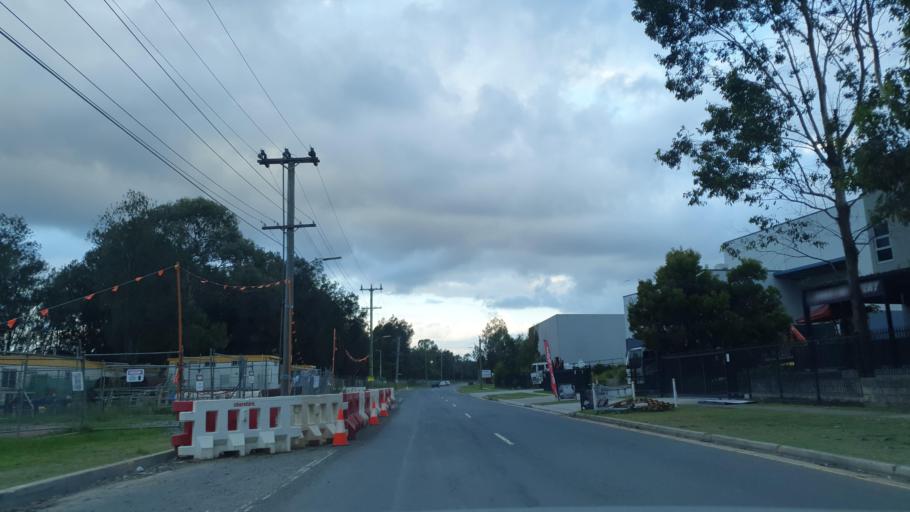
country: AU
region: New South Wales
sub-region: Penrith Municipality
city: Werrington County
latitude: -33.7373
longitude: 150.7689
